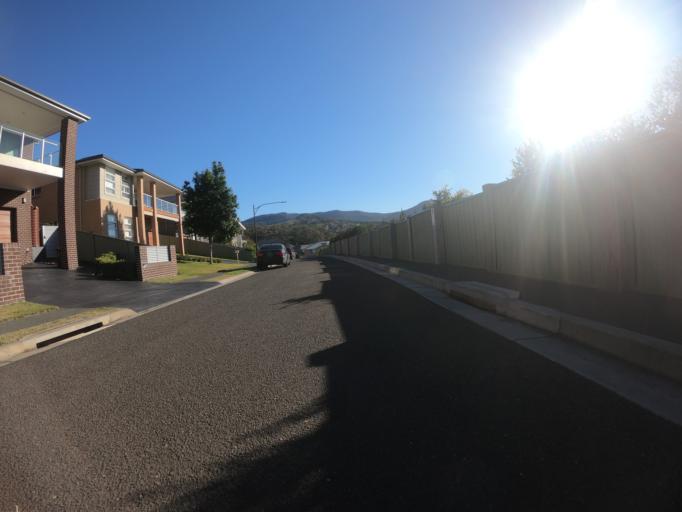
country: AU
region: New South Wales
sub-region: Wollongong
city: Cordeaux Heights
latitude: -34.4399
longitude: 150.8443
